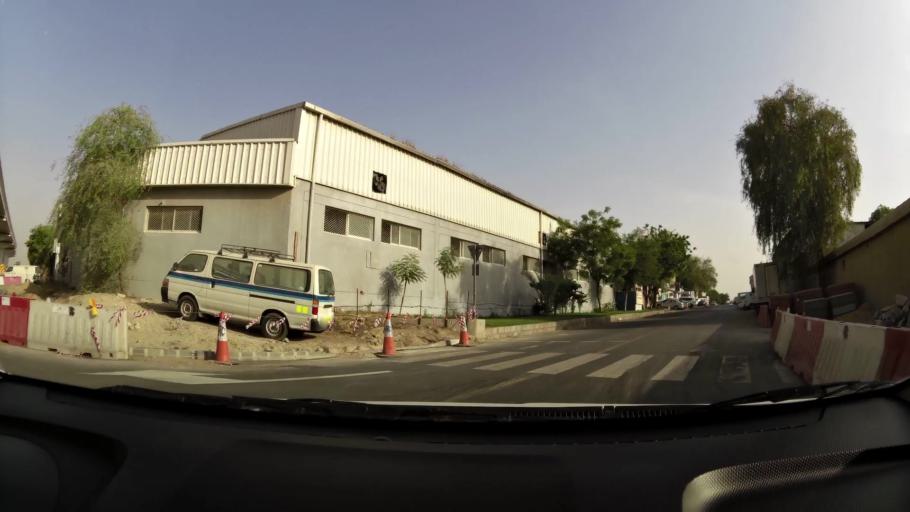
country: AE
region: Ash Shariqah
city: Sharjah
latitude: 25.2363
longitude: 55.3749
